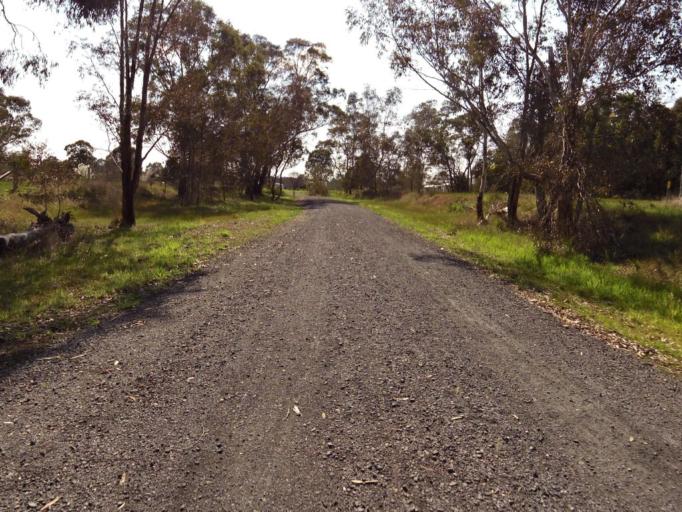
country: AU
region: Victoria
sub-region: Murrindindi
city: Alexandra
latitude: -37.1033
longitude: 145.6176
